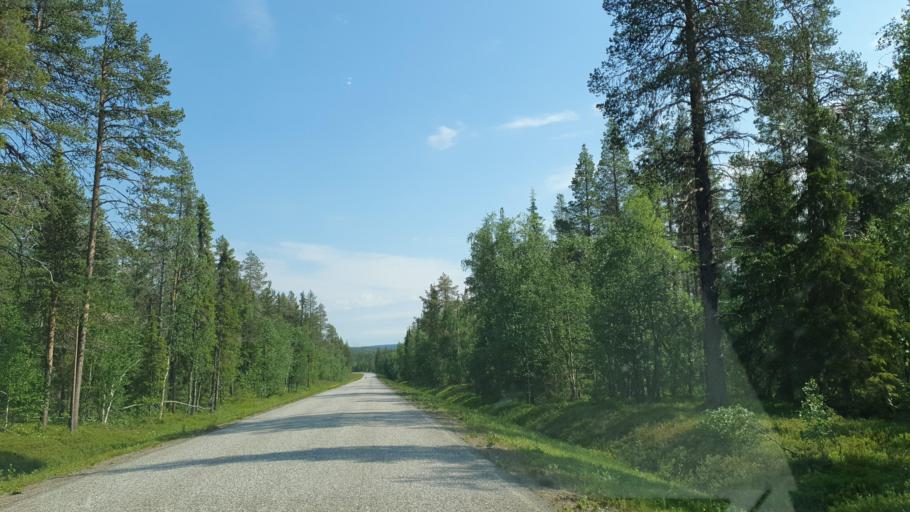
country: FI
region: Lapland
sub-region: Tunturi-Lappi
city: Muonio
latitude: 67.9269
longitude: 24.1373
